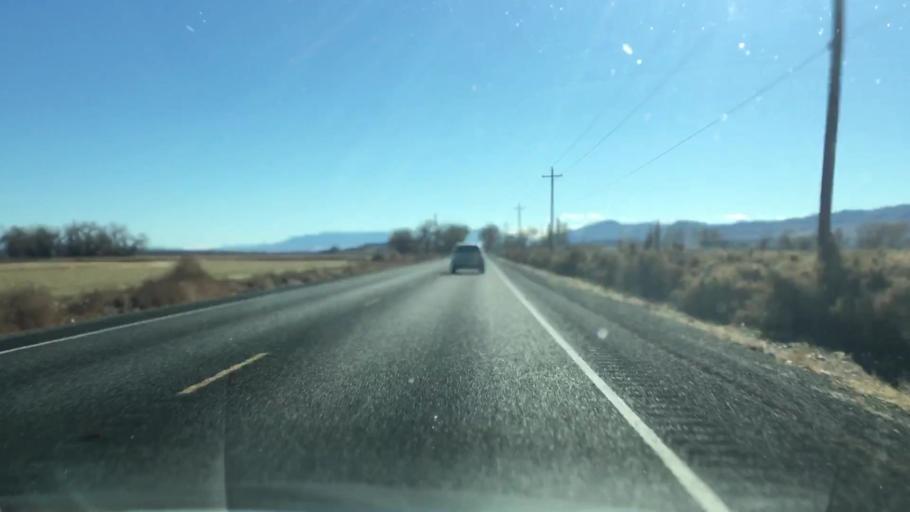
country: US
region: Nevada
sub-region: Lyon County
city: Yerington
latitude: 39.0560
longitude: -119.1814
